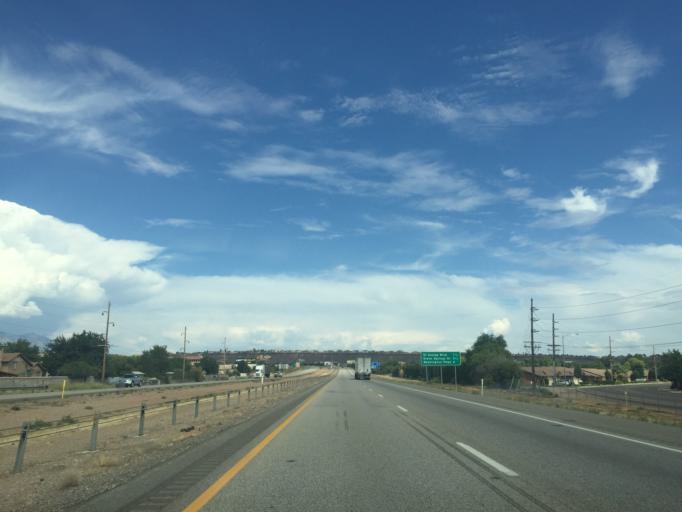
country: US
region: Utah
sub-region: Washington County
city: Saint George
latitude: 37.0920
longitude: -113.5722
